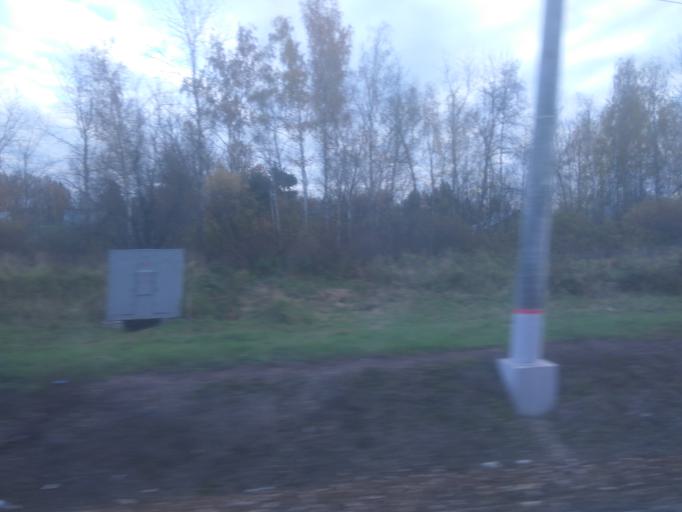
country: RU
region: Moskovskaya
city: Kokoshkino
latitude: 55.5957
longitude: 37.1614
